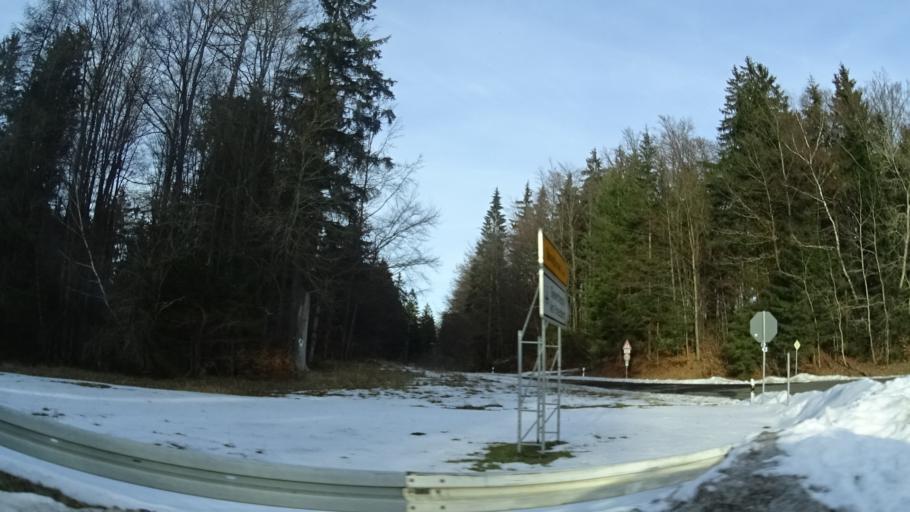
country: DE
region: Bavaria
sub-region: Regierungsbezirk Unterfranken
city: Wildflecken
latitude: 50.3650
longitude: 9.9209
